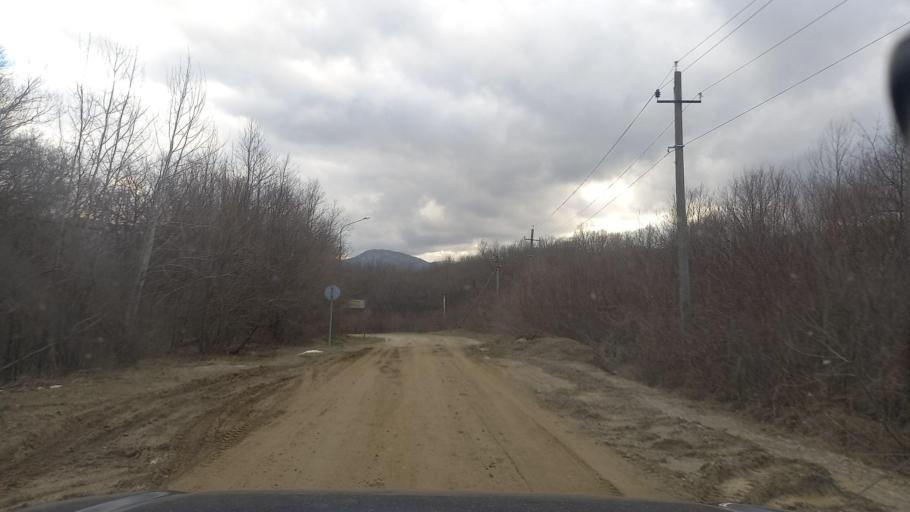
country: RU
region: Krasnodarskiy
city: Smolenskaya
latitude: 44.5721
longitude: 38.8073
